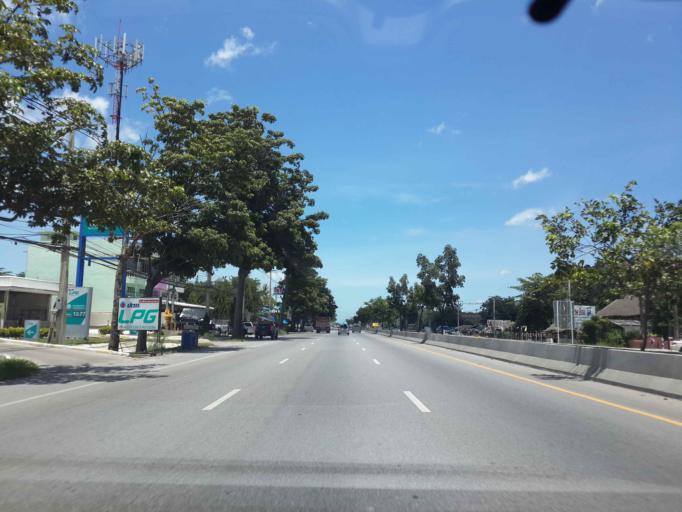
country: TH
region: Phetchaburi
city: Cha-am
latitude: 12.8234
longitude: 99.9379
